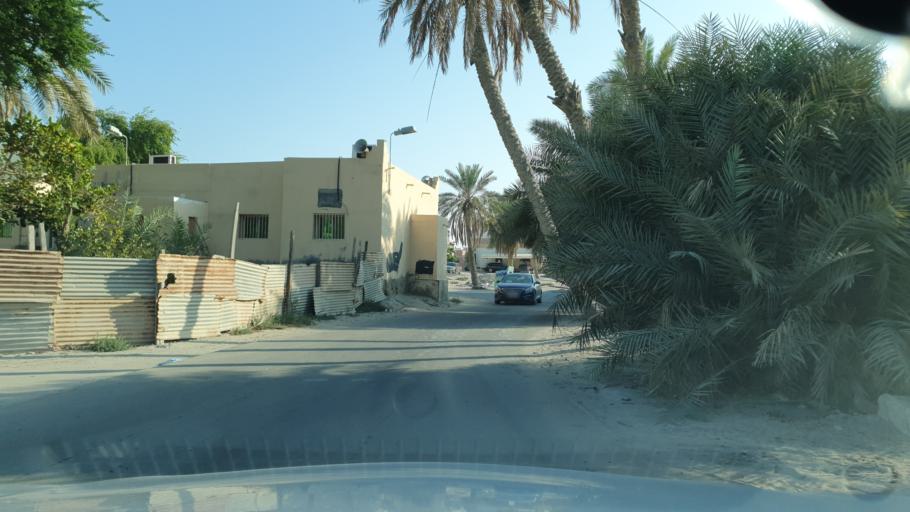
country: BH
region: Manama
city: Jidd Hafs
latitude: 26.2202
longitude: 50.4637
